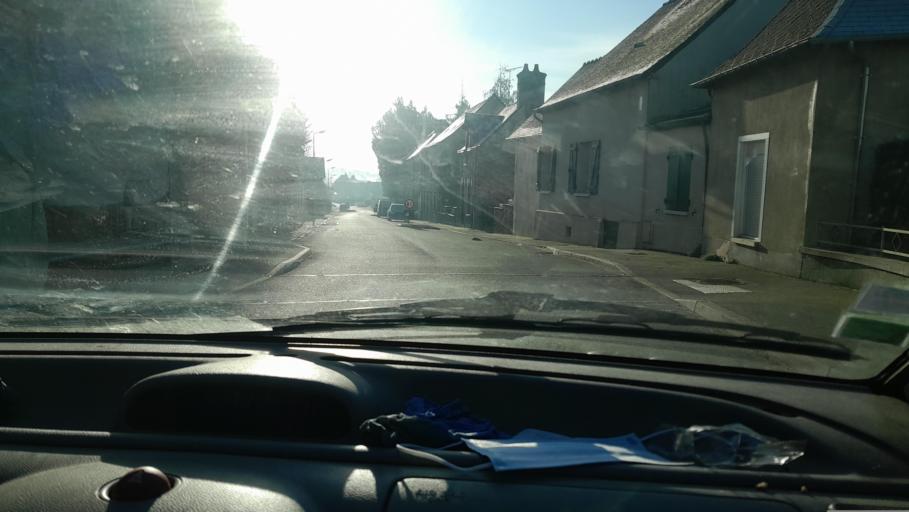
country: FR
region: Brittany
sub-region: Departement d'Ille-et-Vilaine
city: Rannee
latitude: 47.8862
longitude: -1.1802
